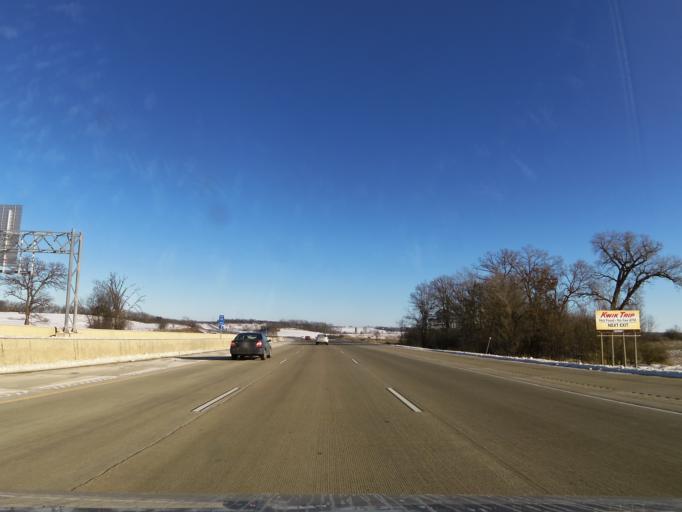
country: US
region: Wisconsin
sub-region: Dane County
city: Cottage Grove
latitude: 43.1032
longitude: -89.2590
